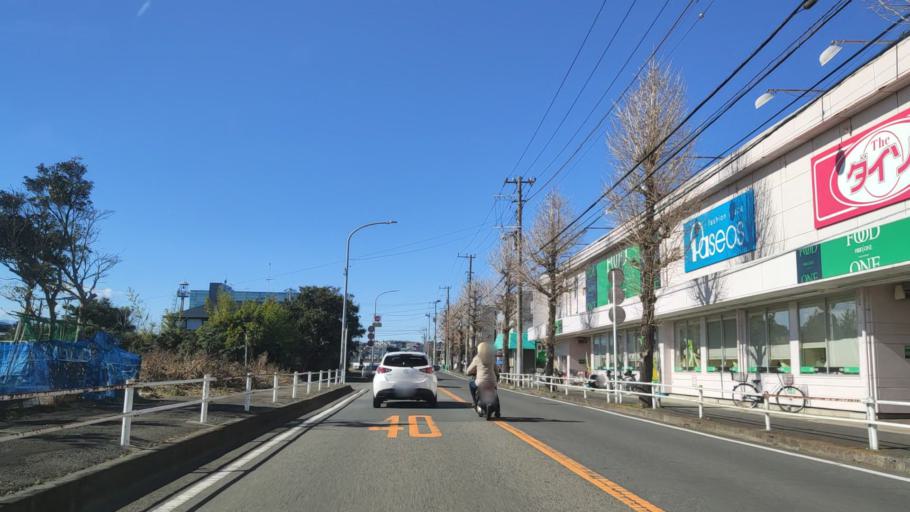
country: JP
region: Tokyo
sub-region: Machida-shi
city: Machida
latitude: 35.5381
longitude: 139.5012
